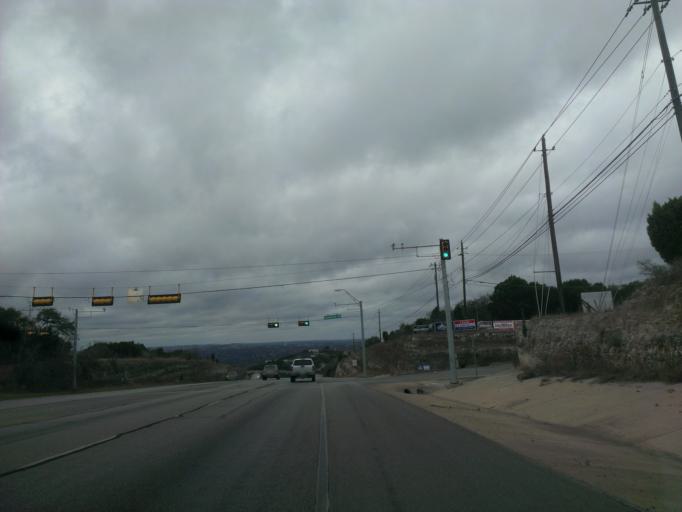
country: US
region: Texas
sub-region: Travis County
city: Hudson Bend
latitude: 30.3946
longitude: -97.8685
